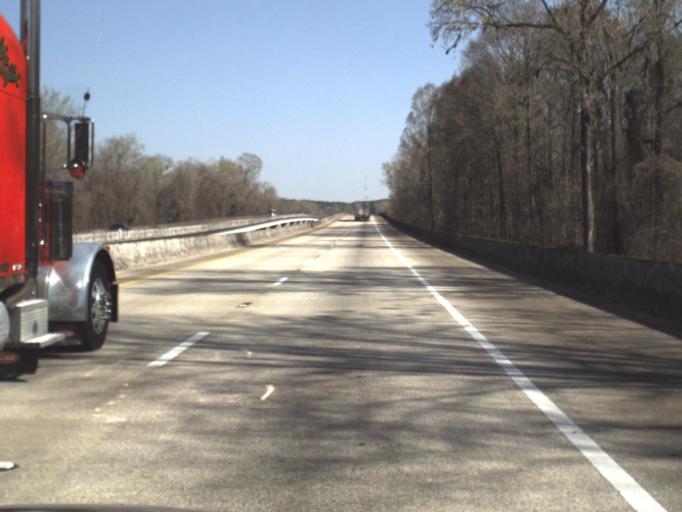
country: US
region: Florida
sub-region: Jackson County
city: Sneads
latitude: 30.6357
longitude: -84.9100
